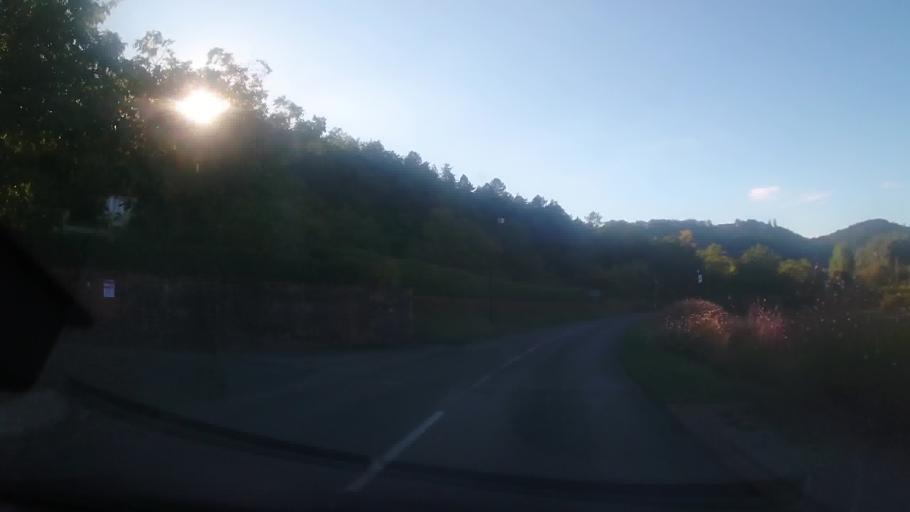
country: FR
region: Aquitaine
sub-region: Departement de la Dordogne
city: Cenac-et-Saint-Julien
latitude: 44.7876
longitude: 1.1669
